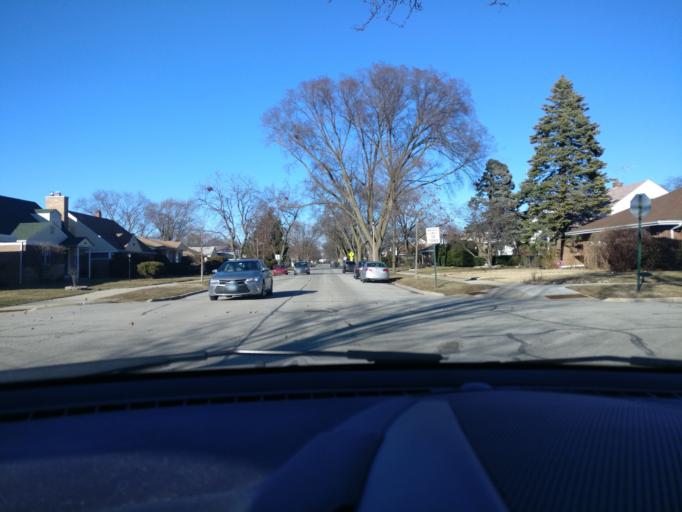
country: US
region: Illinois
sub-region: Cook County
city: Skokie
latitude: 42.0353
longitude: -87.7570
